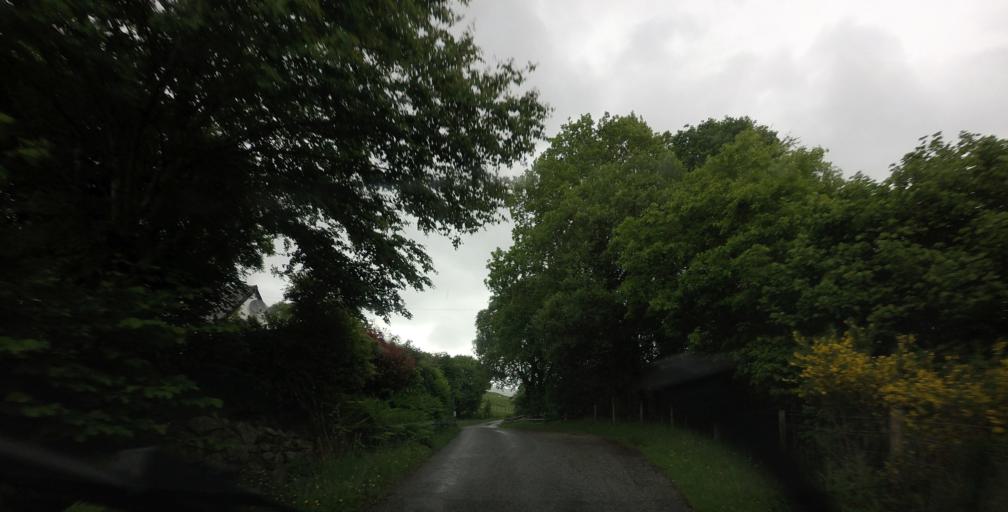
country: GB
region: Scotland
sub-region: Argyll and Bute
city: Oban
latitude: 56.7114
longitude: -5.5635
